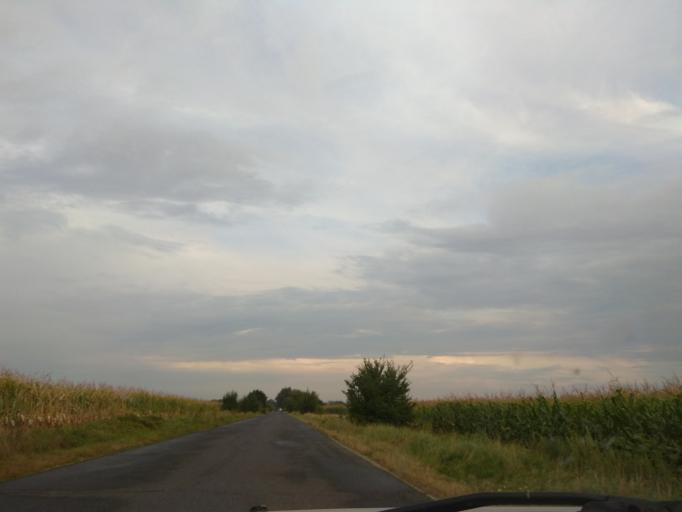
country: HU
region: Borsod-Abauj-Zemplen
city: Felsozsolca
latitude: 48.0928
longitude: 20.8352
